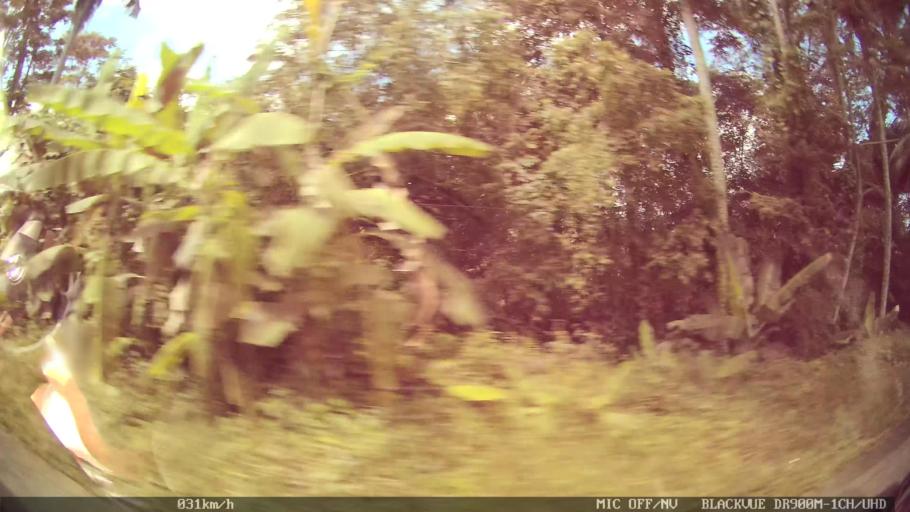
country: ID
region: Bali
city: Banjar Apuan Kaja
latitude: -8.4979
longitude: 115.3412
